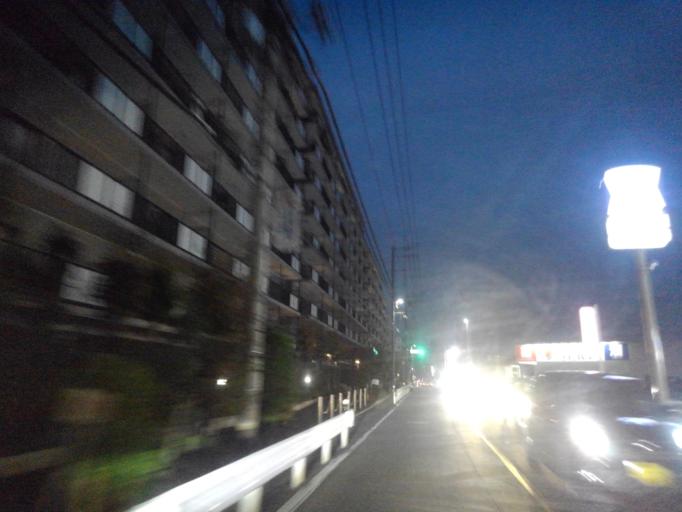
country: JP
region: Saitama
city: Tokorozawa
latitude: 35.8124
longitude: 139.4482
